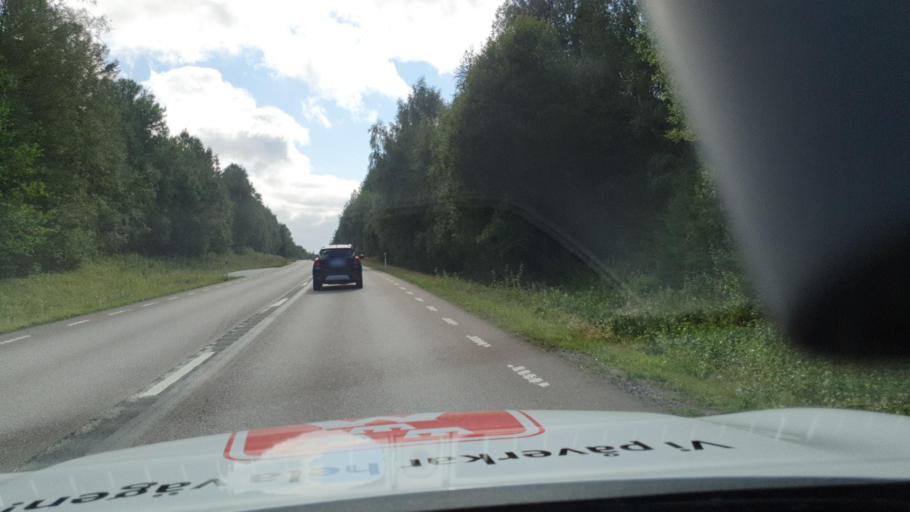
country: SE
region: Vaestra Goetaland
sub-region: Bengtsfors Kommun
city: Billingsfors
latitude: 58.9361
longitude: 12.1872
